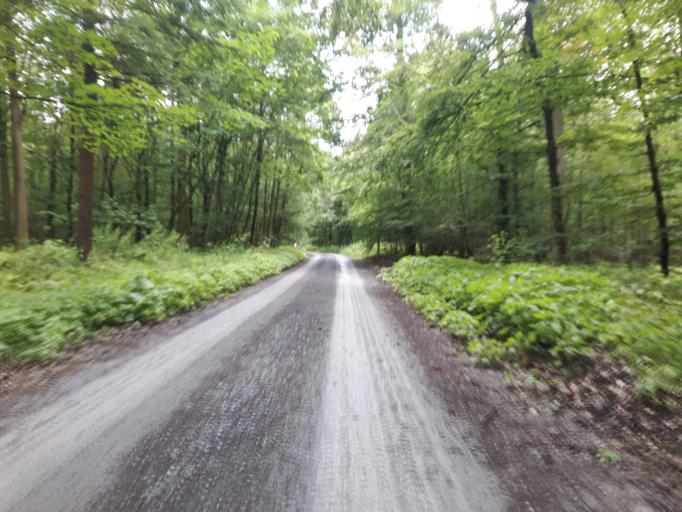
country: DE
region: Baden-Wuerttemberg
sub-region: Regierungsbezirk Stuttgart
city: Eppingen
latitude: 49.1126
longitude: 8.9419
